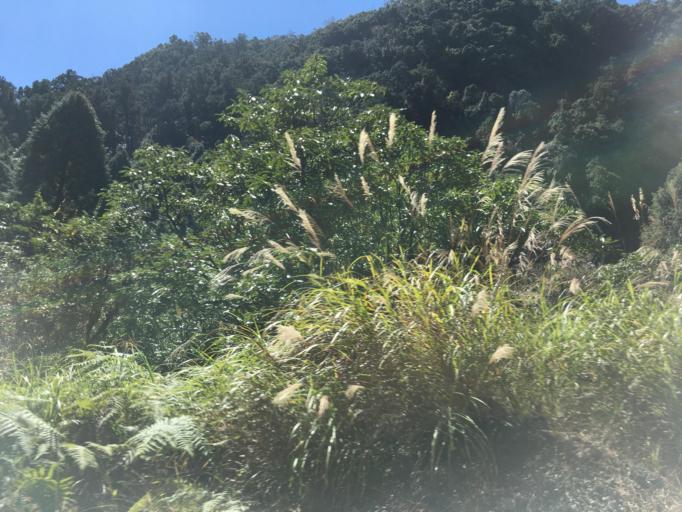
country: TW
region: Taiwan
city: Daxi
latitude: 24.5763
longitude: 121.4126
